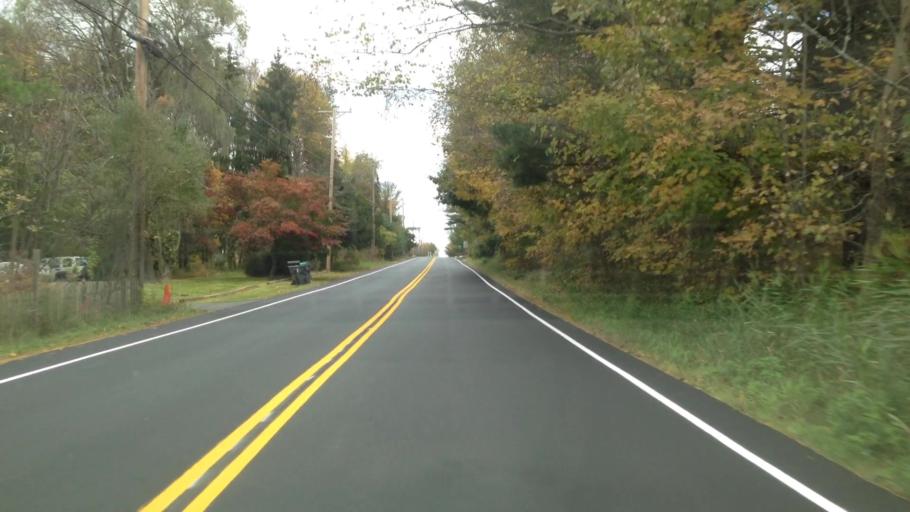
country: US
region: New York
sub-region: Ulster County
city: New Paltz
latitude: 41.7359
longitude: -74.0918
